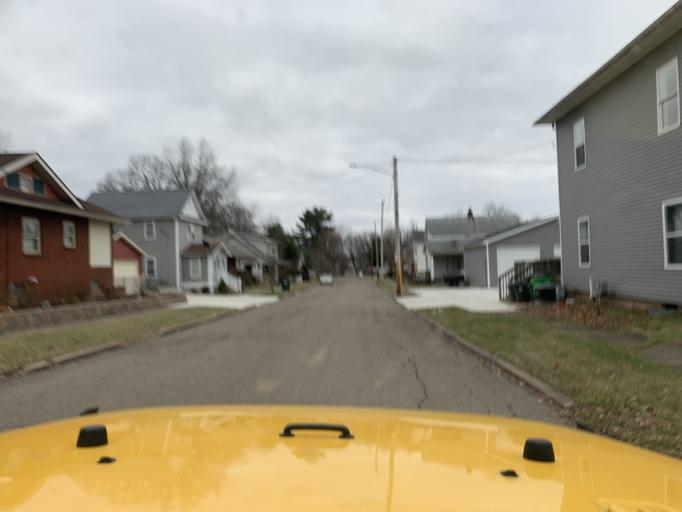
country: US
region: Ohio
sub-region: Tuscarawas County
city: Dover
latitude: 40.5242
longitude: -81.4715
